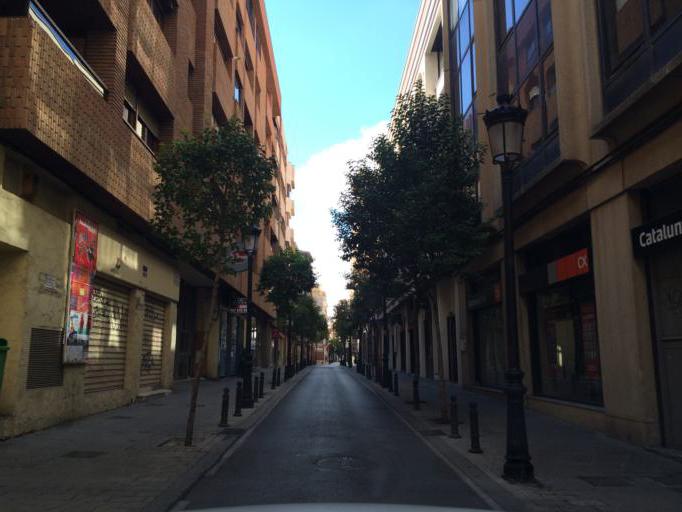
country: ES
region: Castille-La Mancha
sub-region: Provincia de Albacete
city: Albacete
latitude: 38.9944
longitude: -1.8533
